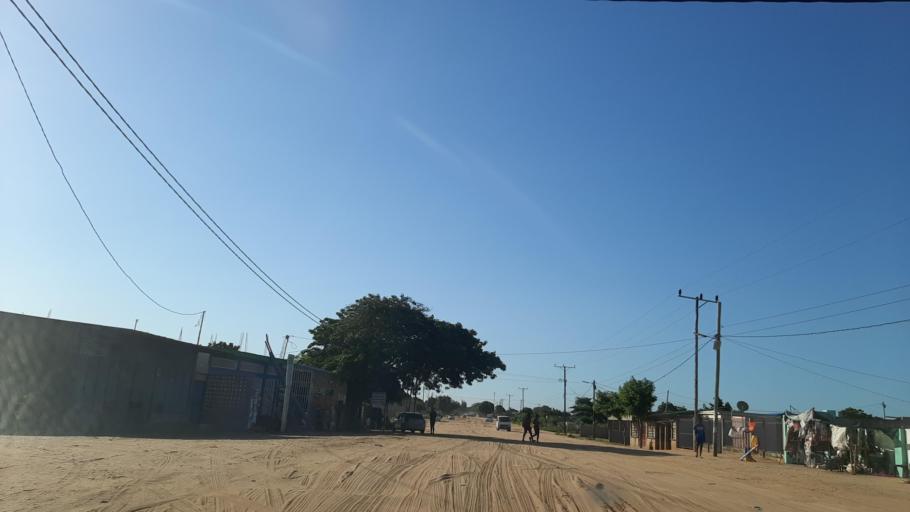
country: MZ
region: Maputo City
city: Maputo
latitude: -25.7502
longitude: 32.5467
